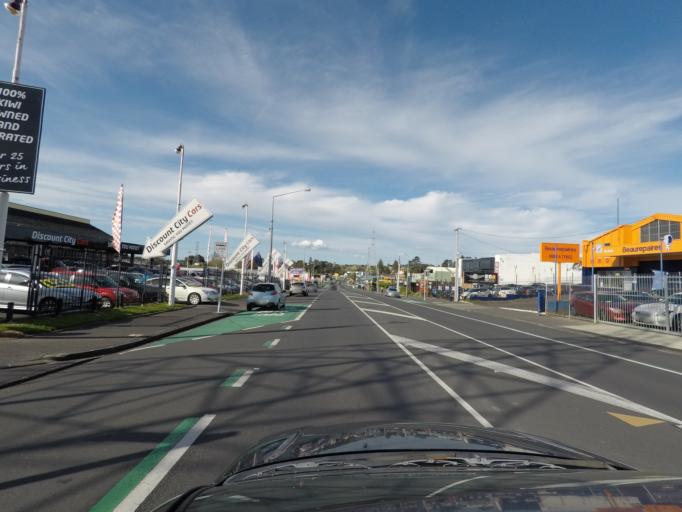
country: NZ
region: Auckland
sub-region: Auckland
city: Waitakere
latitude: -36.9049
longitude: 174.6869
